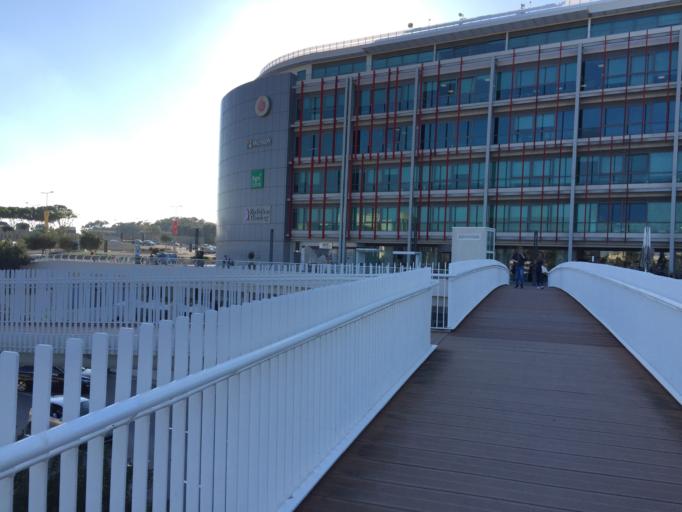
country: MT
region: Il-Gudja
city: Gudja
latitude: 35.8510
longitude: 14.4952
